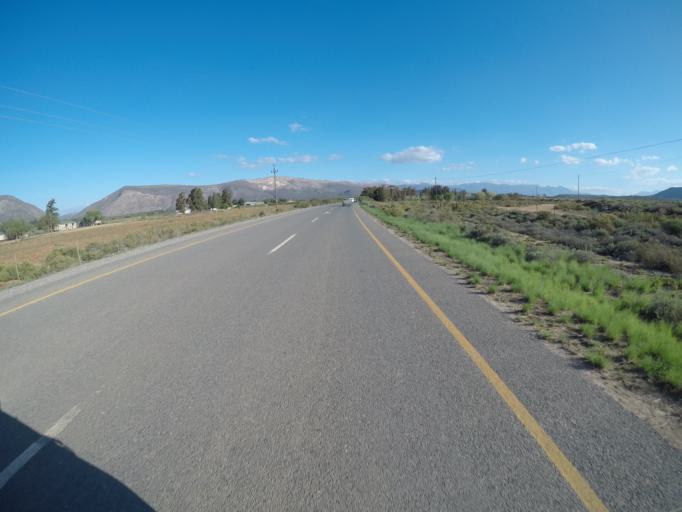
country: ZA
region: Western Cape
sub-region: Cape Winelands District Municipality
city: Ashton
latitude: -33.8068
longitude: 19.7823
